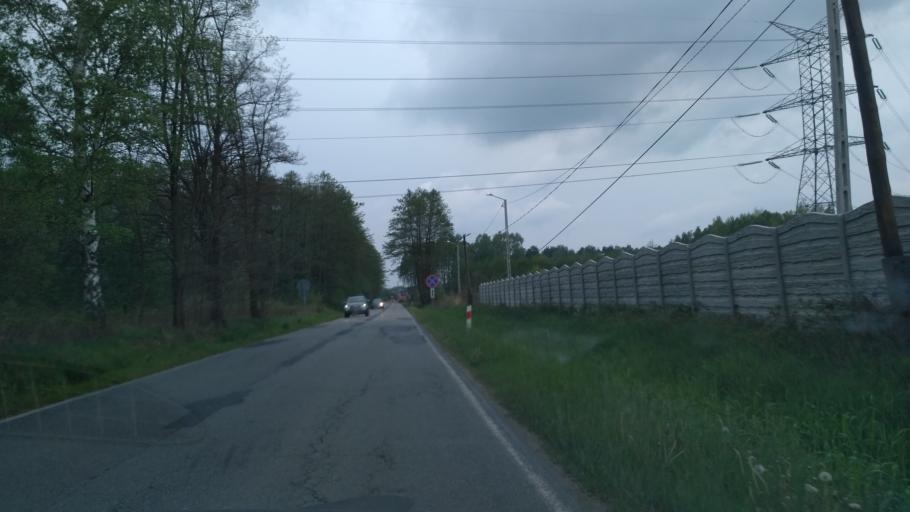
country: PL
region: Subcarpathian Voivodeship
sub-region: Powiat kolbuszowski
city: Kolbuszowa
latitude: 50.1867
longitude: 21.7620
